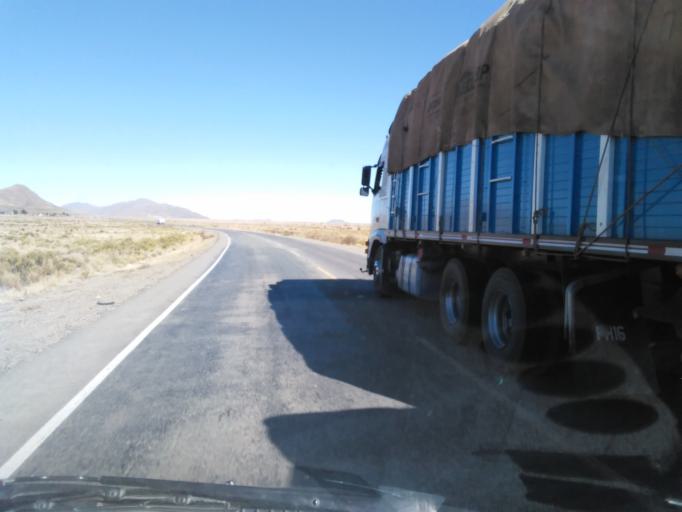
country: BO
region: Oruro
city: Machacamarca
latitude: -18.0904
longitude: -67.0105
